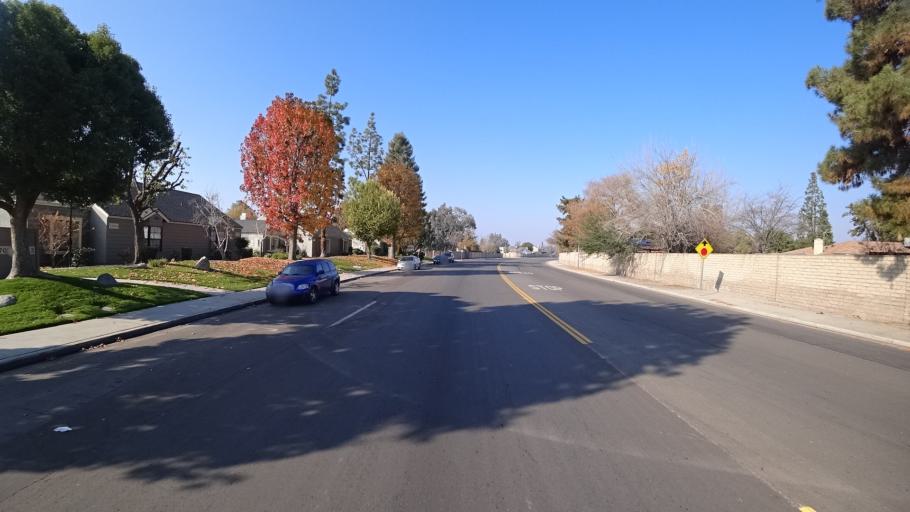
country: US
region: California
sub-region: Kern County
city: Greenacres
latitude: 35.3224
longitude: -119.0796
